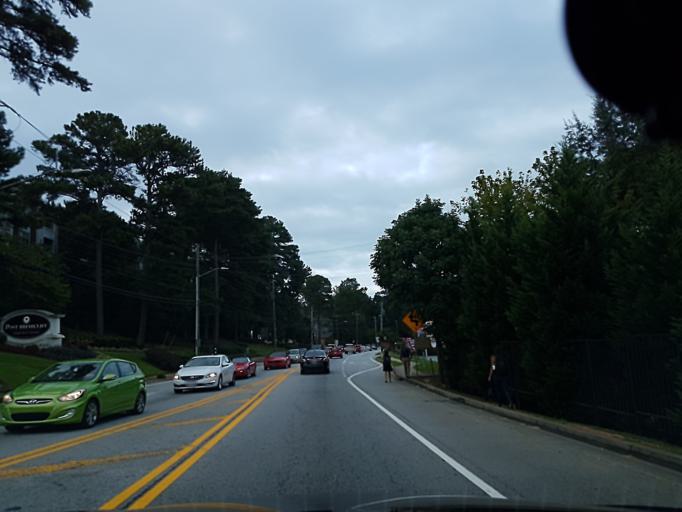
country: US
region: Georgia
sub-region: DeKalb County
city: North Druid Hills
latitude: 33.8150
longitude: -84.3344
